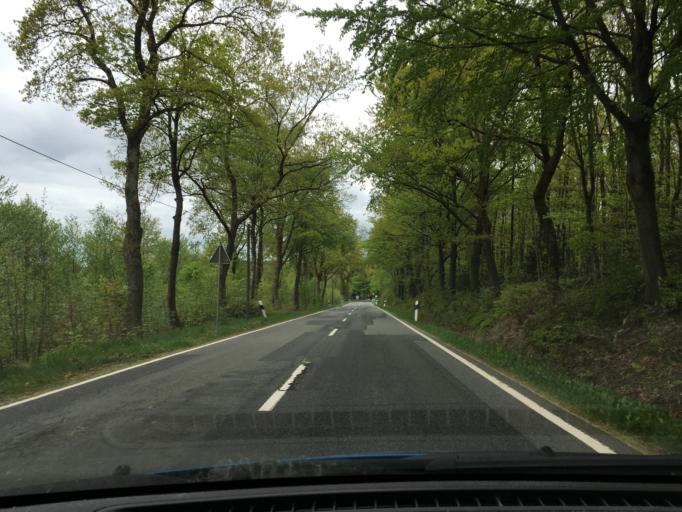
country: DE
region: Lower Saxony
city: Arholzen
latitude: 51.7700
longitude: 9.5551
